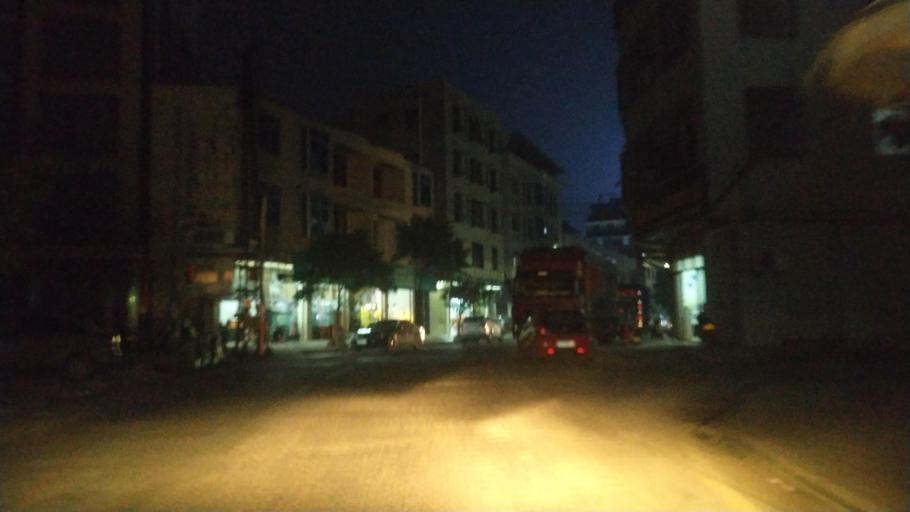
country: CN
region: Guangdong
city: Xiaguo
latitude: 21.6468
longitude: 110.6310
